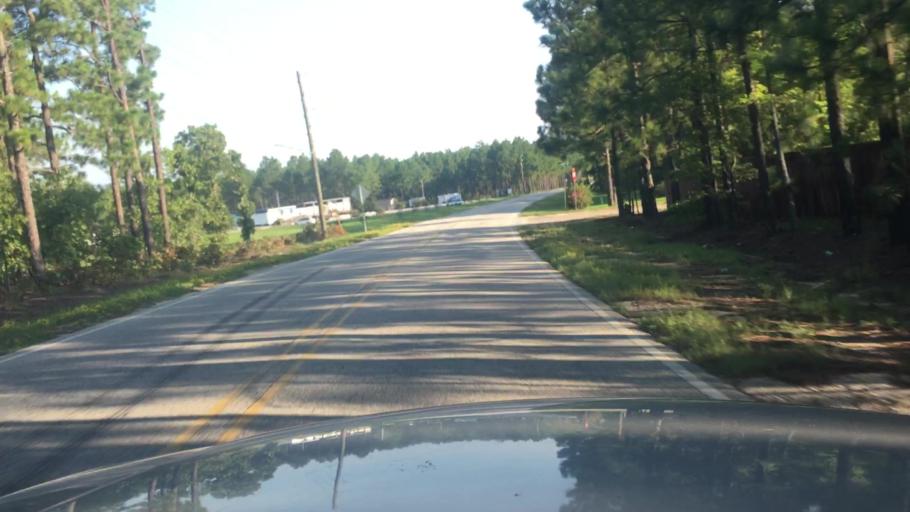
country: US
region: North Carolina
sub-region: Harnett County
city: Walkertown
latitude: 35.2134
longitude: -78.8643
